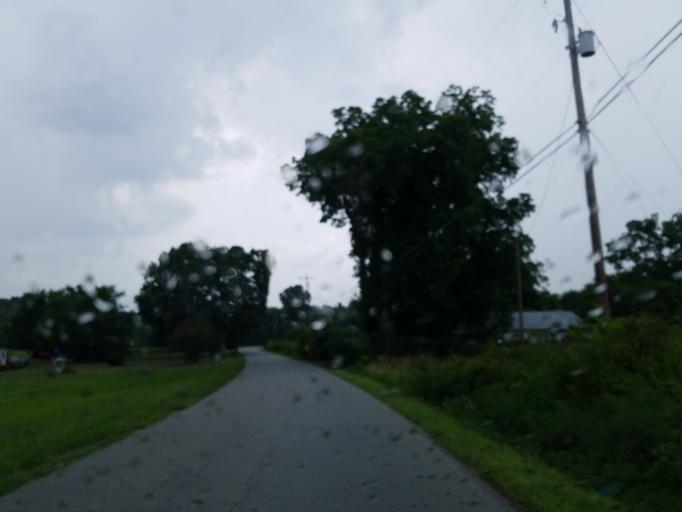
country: US
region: Georgia
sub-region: Bartow County
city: Rydal
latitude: 34.2768
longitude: -84.7543
